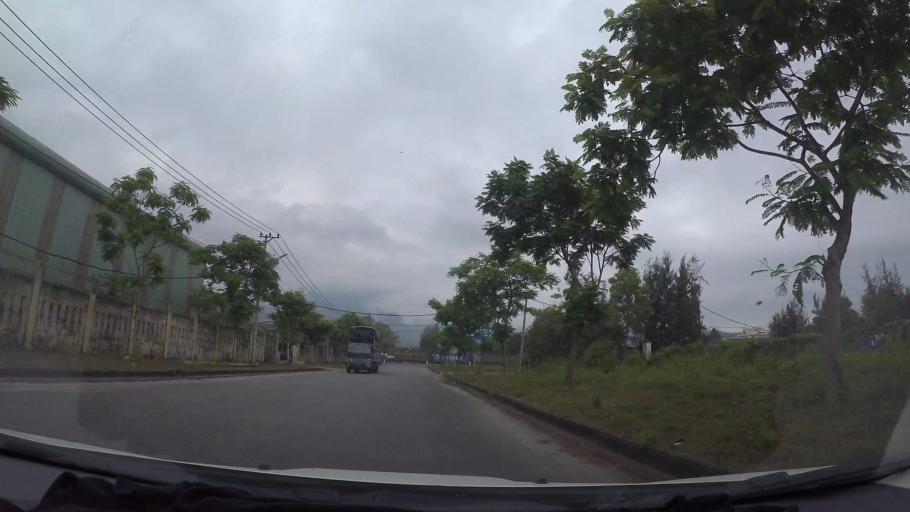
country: VN
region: Da Nang
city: Lien Chieu
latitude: 16.1269
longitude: 108.1173
